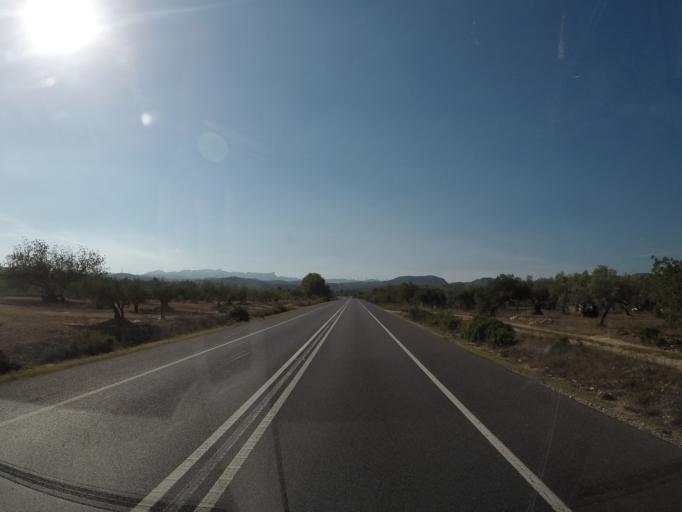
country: ES
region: Catalonia
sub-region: Provincia de Tarragona
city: El Perello
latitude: 40.8971
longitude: 0.7399
